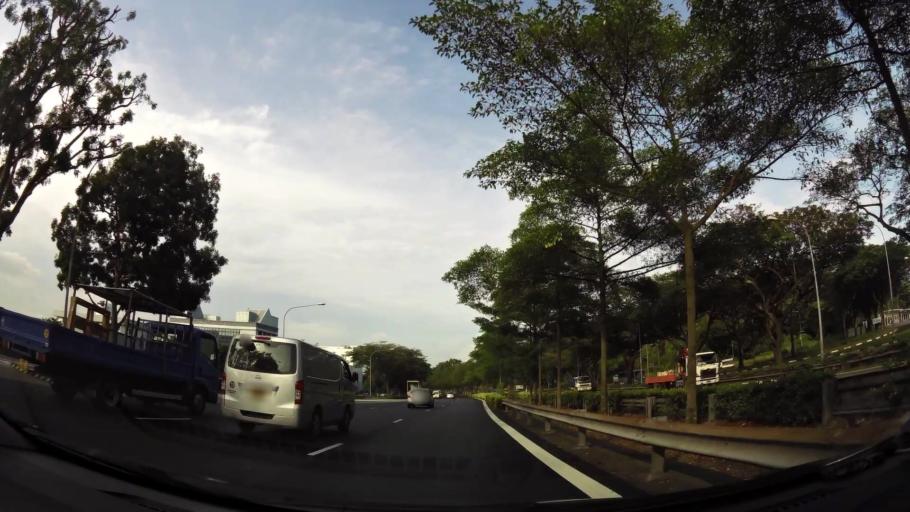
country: MY
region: Johor
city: Johor Bahru
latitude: 1.3302
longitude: 103.6731
